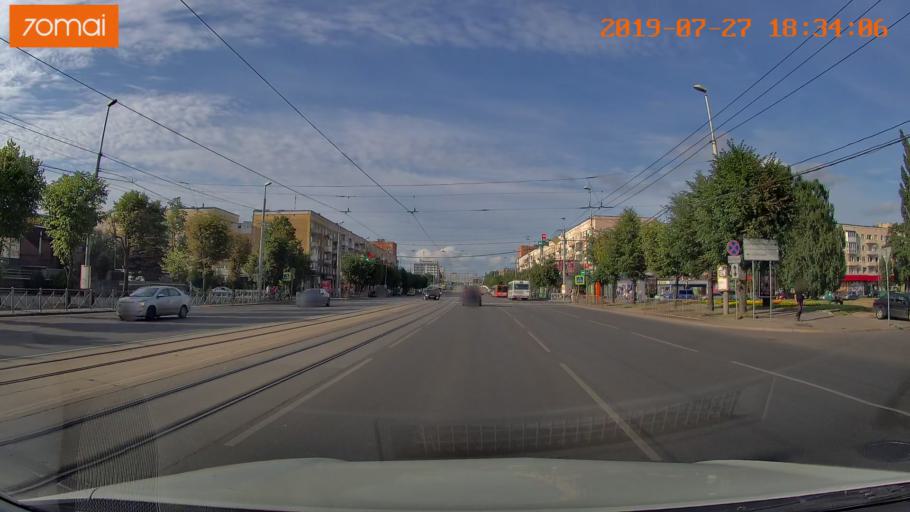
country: RU
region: Kaliningrad
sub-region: Gorod Kaliningrad
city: Kaliningrad
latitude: 54.7018
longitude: 20.5046
